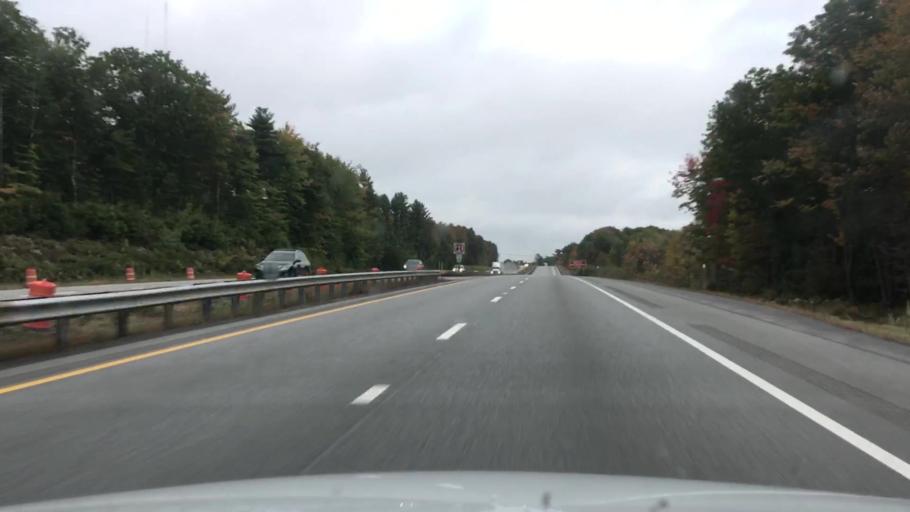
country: US
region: Maine
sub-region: Cumberland County
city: Cumberland Center
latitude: 43.8443
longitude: -70.3239
